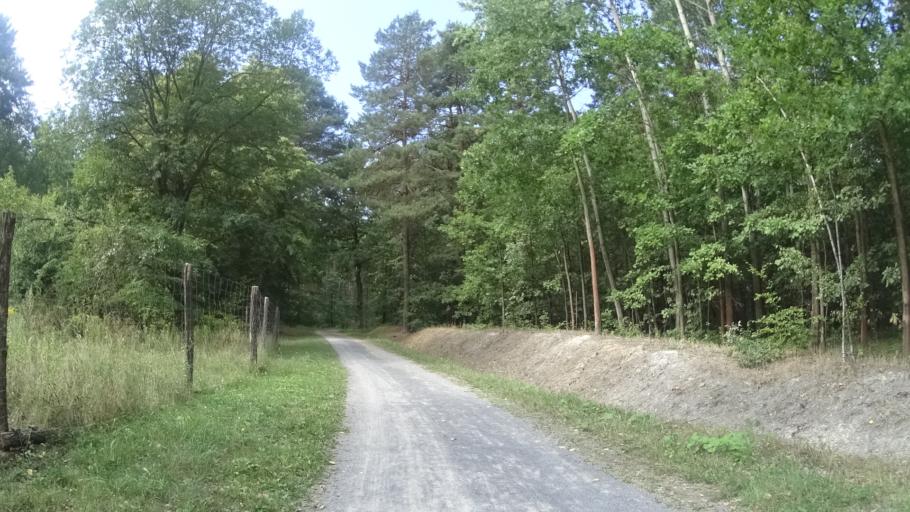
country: PL
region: Lubusz
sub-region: Powiat zarski
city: Leknica
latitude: 51.5355
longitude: 14.7546
